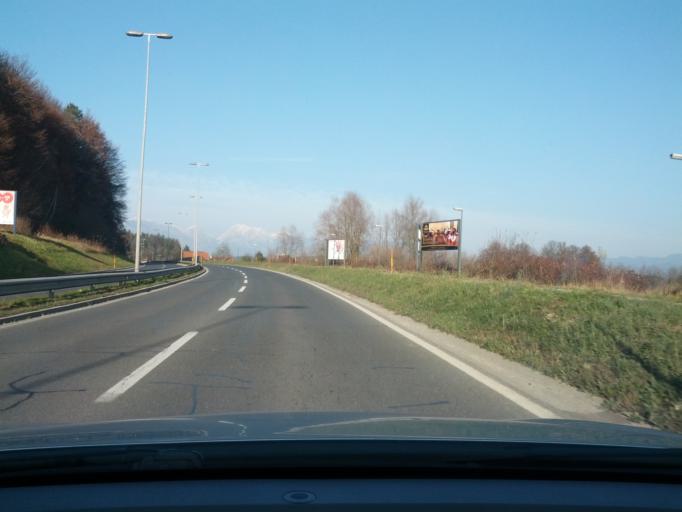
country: SI
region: Trzin
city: Trzin
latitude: 46.1070
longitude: 14.5453
